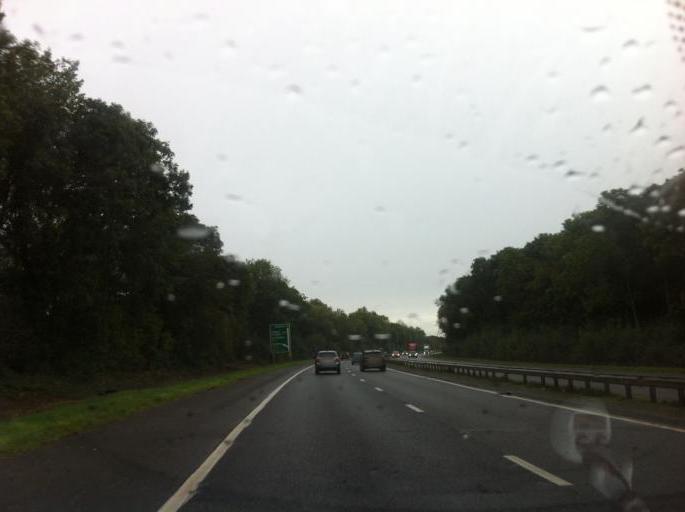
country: GB
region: England
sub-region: Peterborough
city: Eye
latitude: 52.5992
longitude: -0.2186
